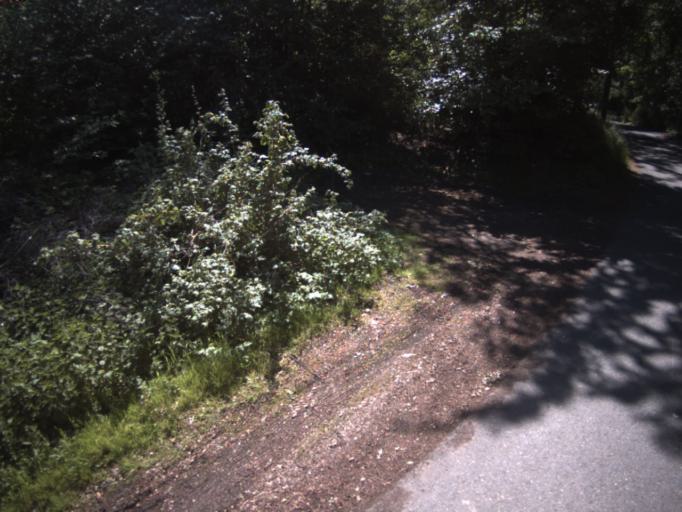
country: SE
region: Skane
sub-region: Helsingborg
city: Rydeback
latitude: 56.0141
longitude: 12.7442
